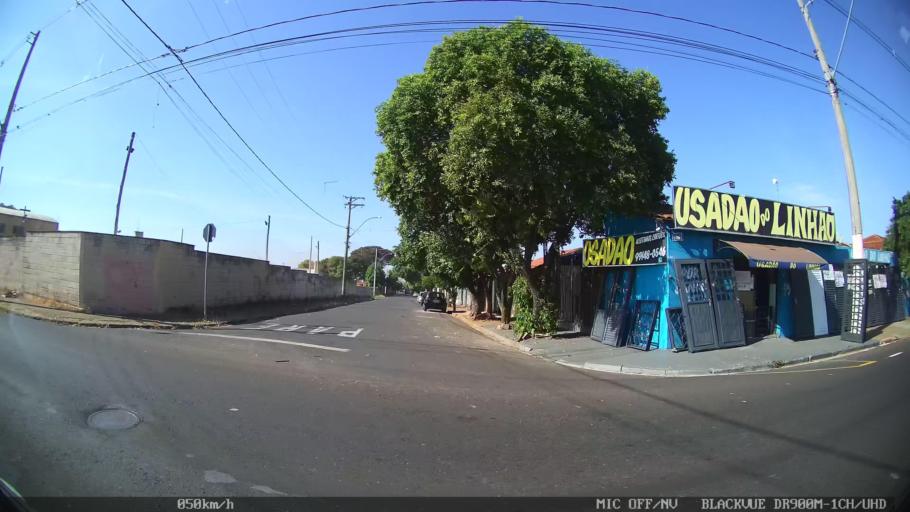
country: BR
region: Sao Paulo
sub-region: Sao Jose Do Rio Preto
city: Sao Jose do Rio Preto
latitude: -20.7810
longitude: -49.4049
